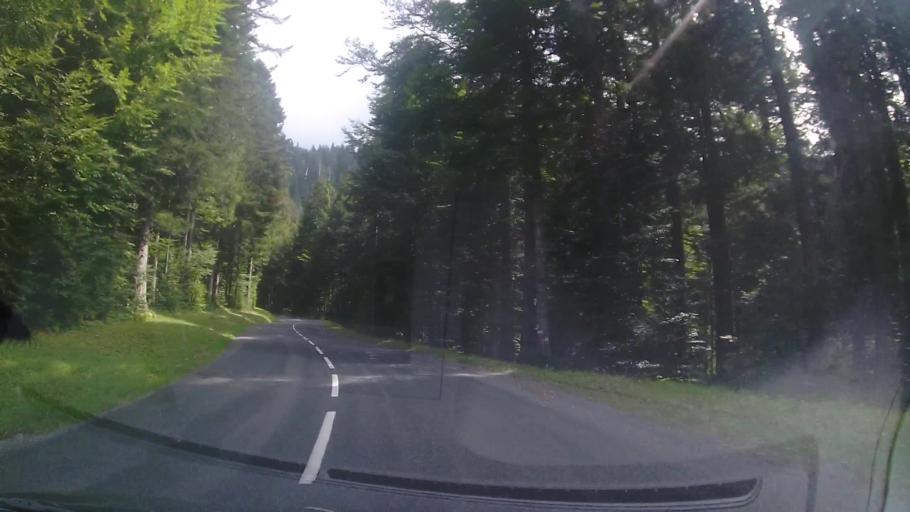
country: FR
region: Rhone-Alpes
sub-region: Departement de l'Ain
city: Gex
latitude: 46.3836
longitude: 6.0442
